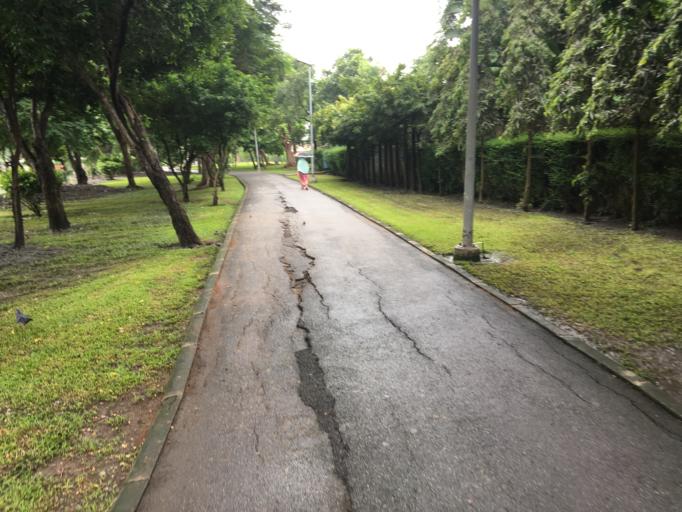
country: TH
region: Bangkok
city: Bueng Kum
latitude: 13.7846
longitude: 100.6715
